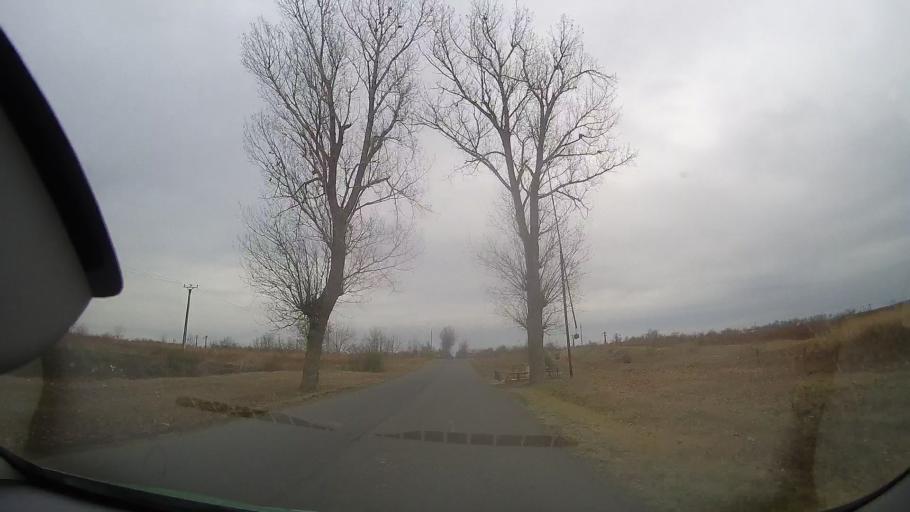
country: RO
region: Braila
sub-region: Comuna Rosiori
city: Rosiori
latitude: 44.8111
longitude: 27.3724
